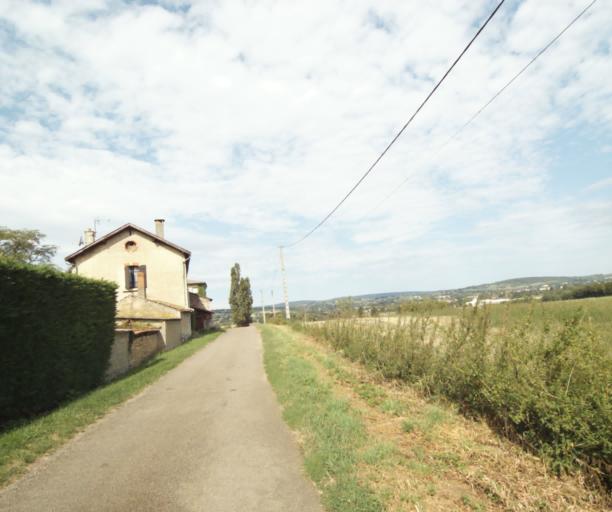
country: FR
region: Bourgogne
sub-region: Departement de Saone-et-Loire
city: Tournus
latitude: 46.5444
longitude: 4.9142
